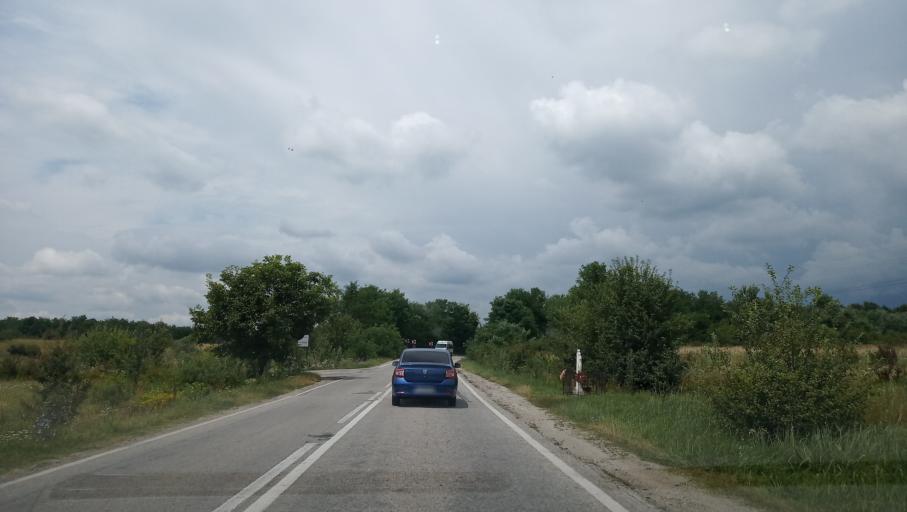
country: RO
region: Gorj
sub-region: Comuna Arcani
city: Arcani
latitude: 45.0826
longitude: 23.1685
